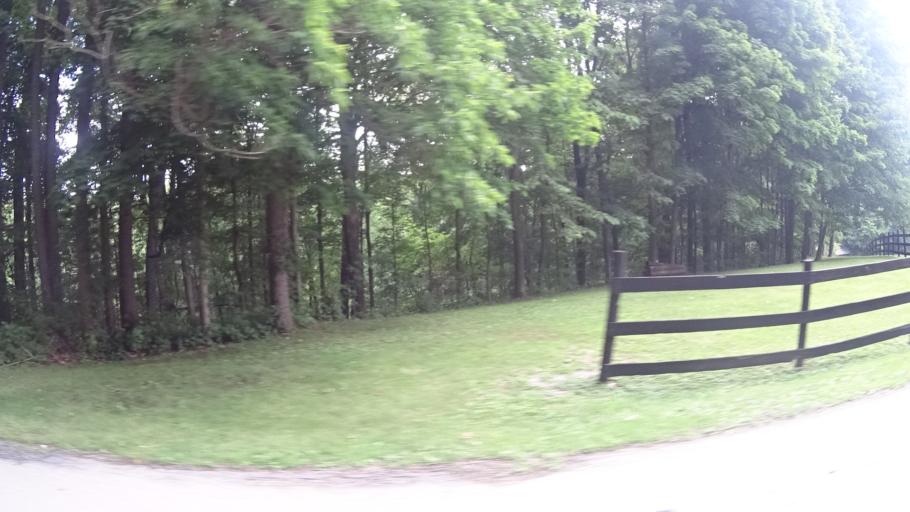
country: US
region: Ohio
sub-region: Lorain County
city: Camden
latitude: 41.2982
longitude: -82.3434
